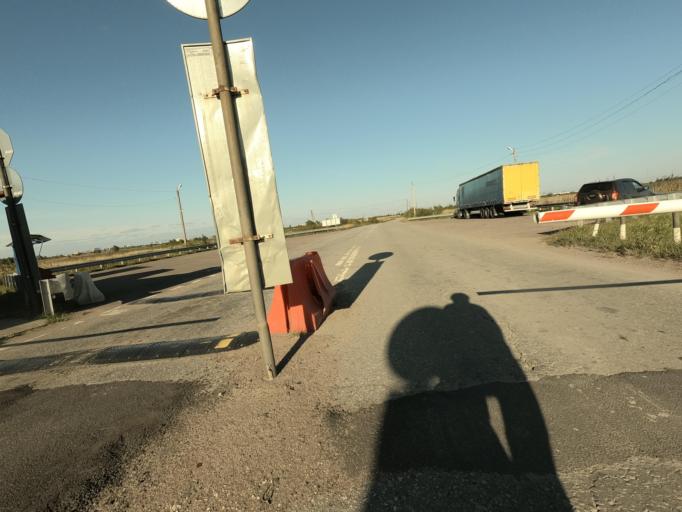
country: RU
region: St.-Petersburg
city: Petro-Slavyanka
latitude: 59.7681
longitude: 30.4914
